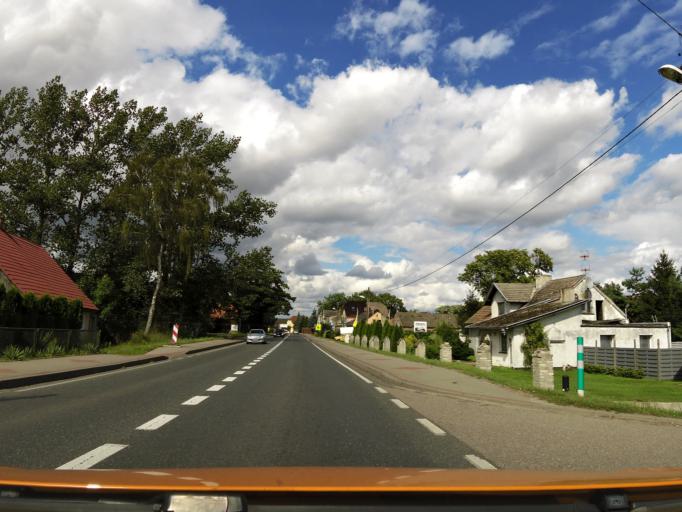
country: PL
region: West Pomeranian Voivodeship
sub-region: Powiat goleniowski
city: Nowogard
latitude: 53.7180
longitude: 15.1892
